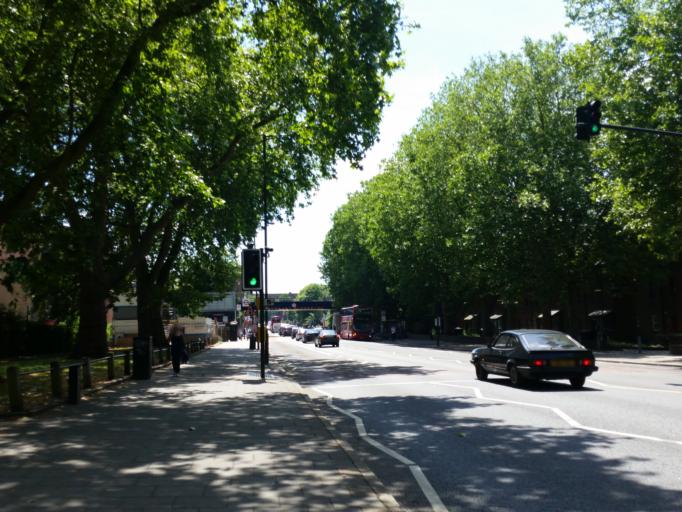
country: GB
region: England
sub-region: Greater London
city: Harringay
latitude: 51.5816
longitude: -0.0724
